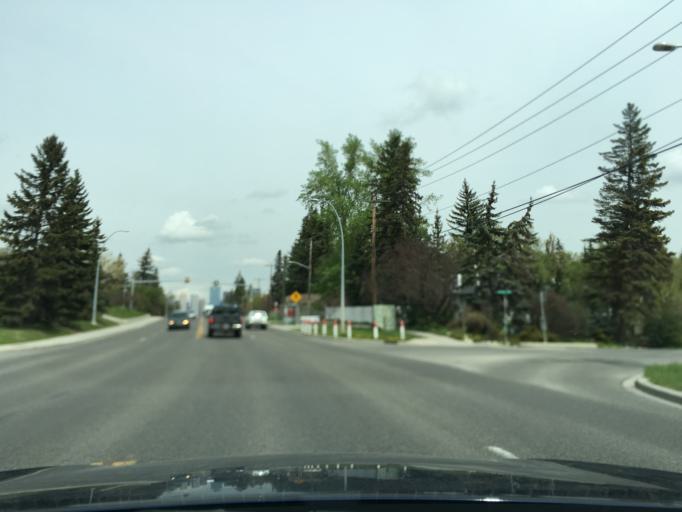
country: CA
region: Alberta
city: Calgary
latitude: 51.0128
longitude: -114.0798
